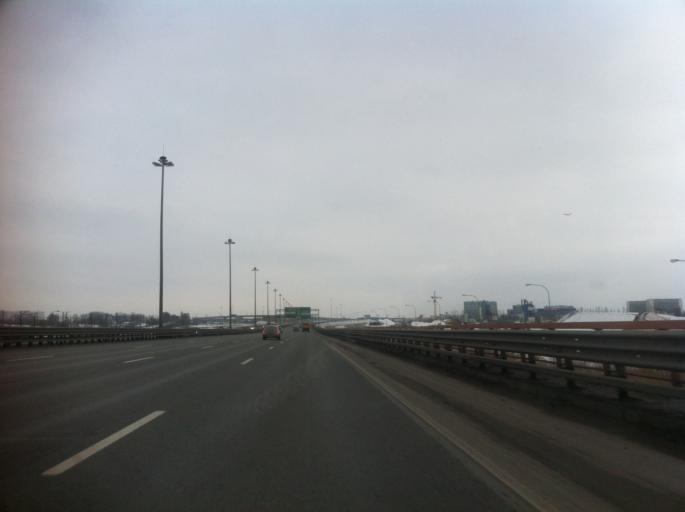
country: RU
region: St.-Petersburg
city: Dachnoye
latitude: 59.8204
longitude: 30.3033
